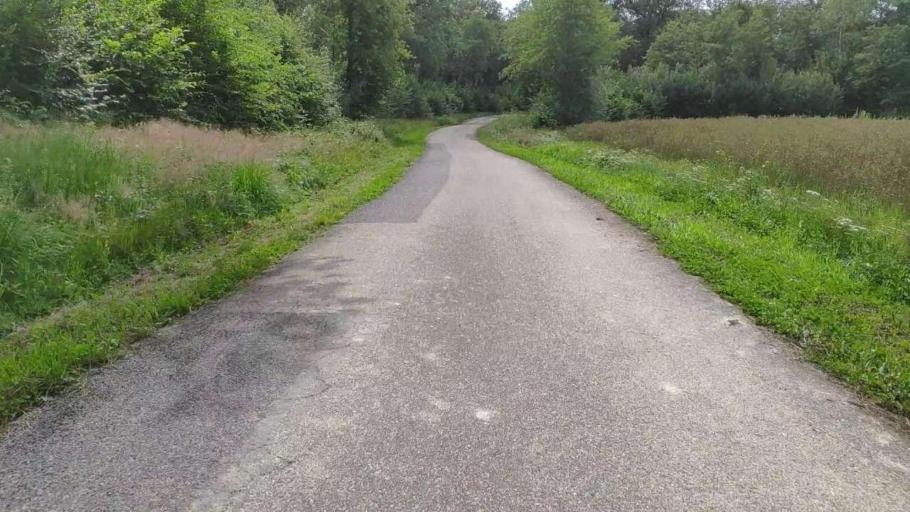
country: FR
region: Franche-Comte
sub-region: Departement du Jura
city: Bletterans
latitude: 46.8143
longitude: 5.4373
